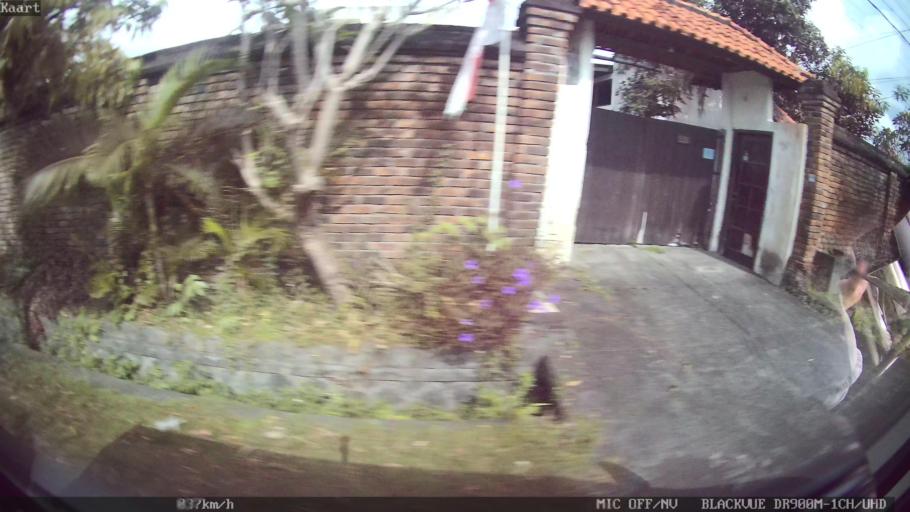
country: ID
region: Bali
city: Banjar Kertasari
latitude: -8.6131
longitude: 115.2002
